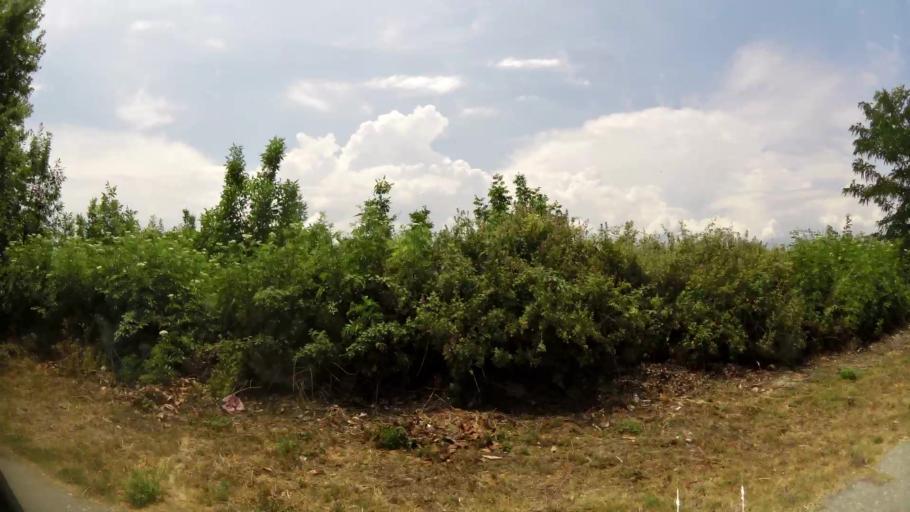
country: GR
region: Central Macedonia
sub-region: Nomos Pierias
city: Peristasi
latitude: 40.2715
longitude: 22.5399
